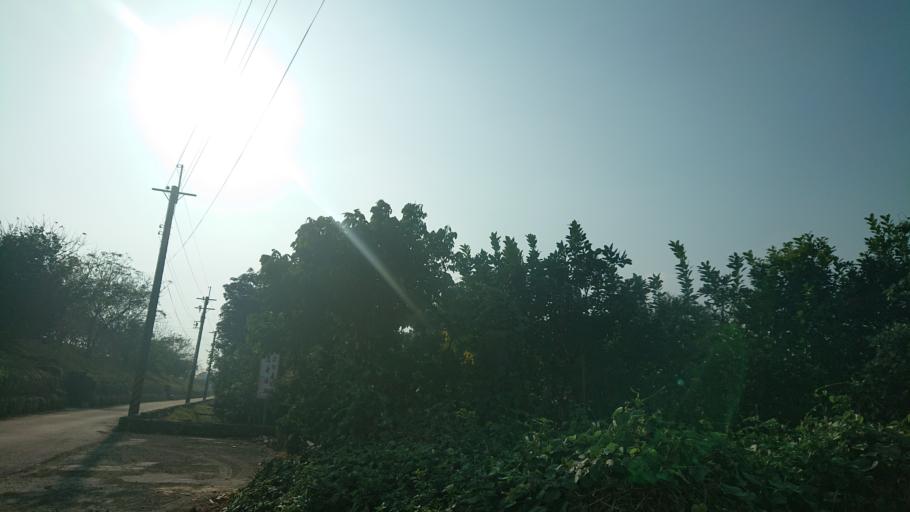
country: TW
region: Taiwan
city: Xinying
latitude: 23.1753
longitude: 120.2607
